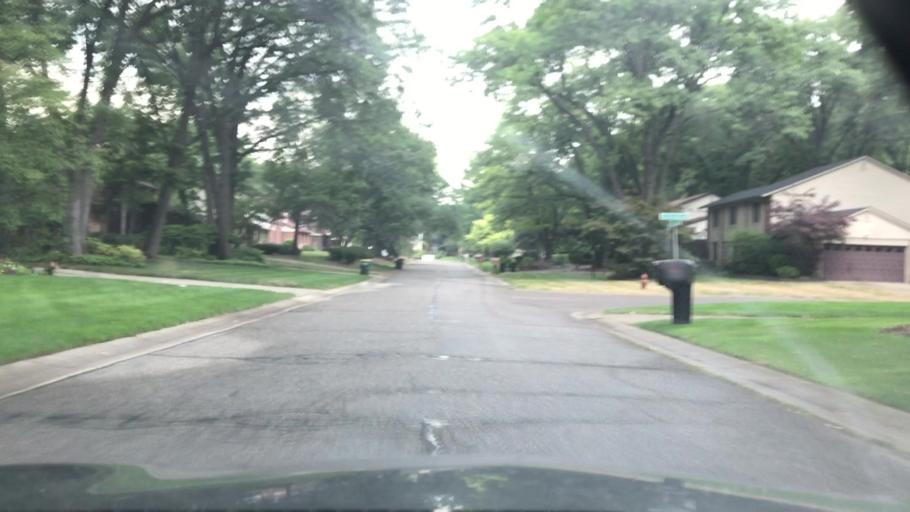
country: US
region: Michigan
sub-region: Oakland County
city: Farmington Hills
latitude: 42.5088
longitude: -83.4038
